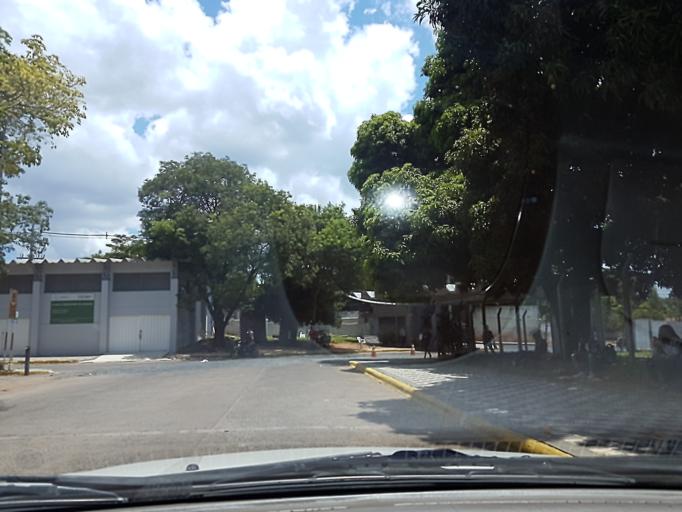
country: PY
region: Asuncion
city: Asuncion
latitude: -25.2728
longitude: -57.5817
